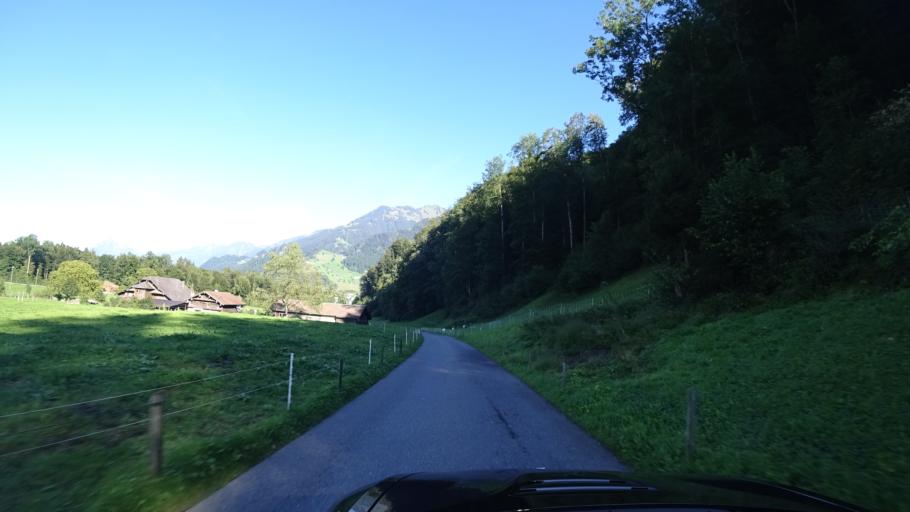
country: CH
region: Obwalden
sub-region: Obwalden
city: Giswil
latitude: 46.8292
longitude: 8.1621
